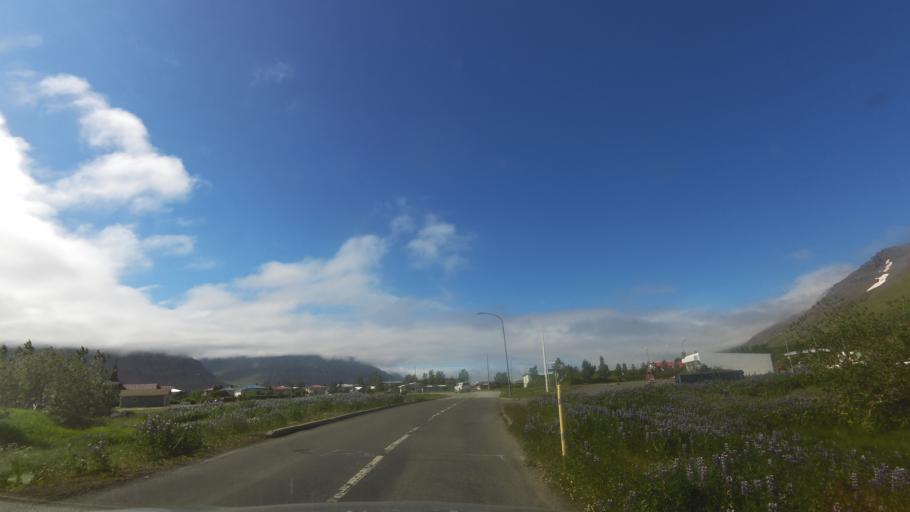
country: IS
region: Westfjords
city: Isafjoerdur
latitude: 66.0514
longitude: -23.5091
